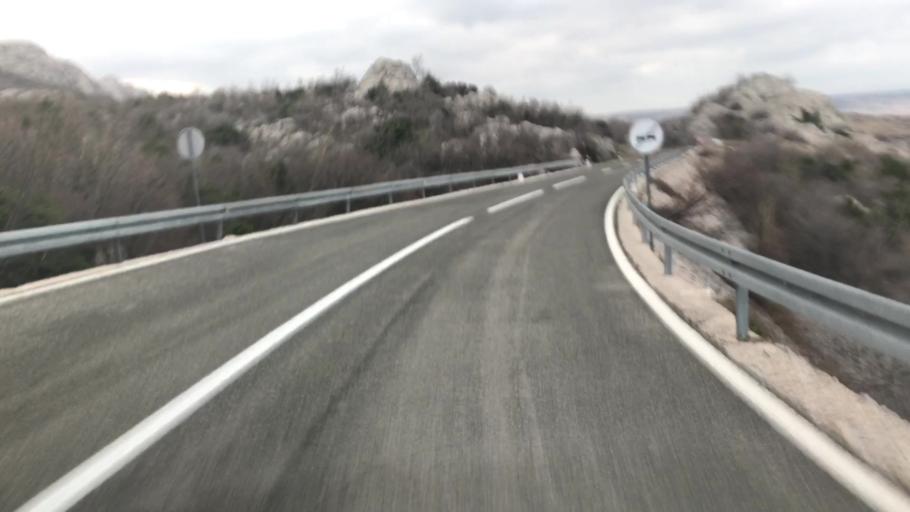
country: HR
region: Licko-Senjska
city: Novalja
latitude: 44.6705
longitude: 14.9439
